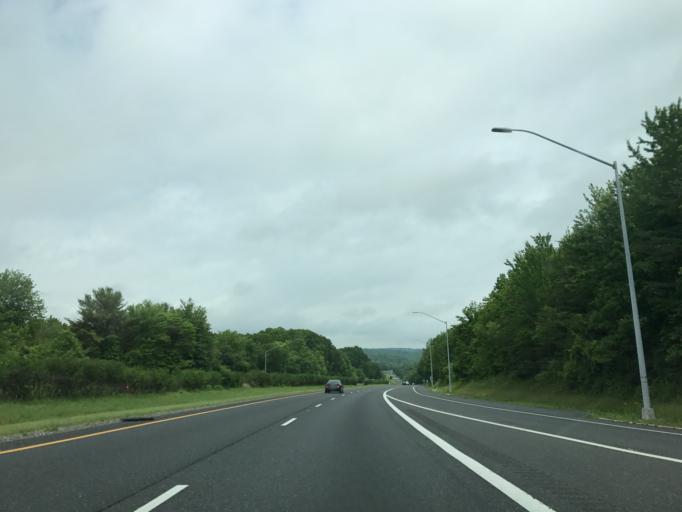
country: US
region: Pennsylvania
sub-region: York County
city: New Freedom
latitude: 39.6353
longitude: -76.6716
